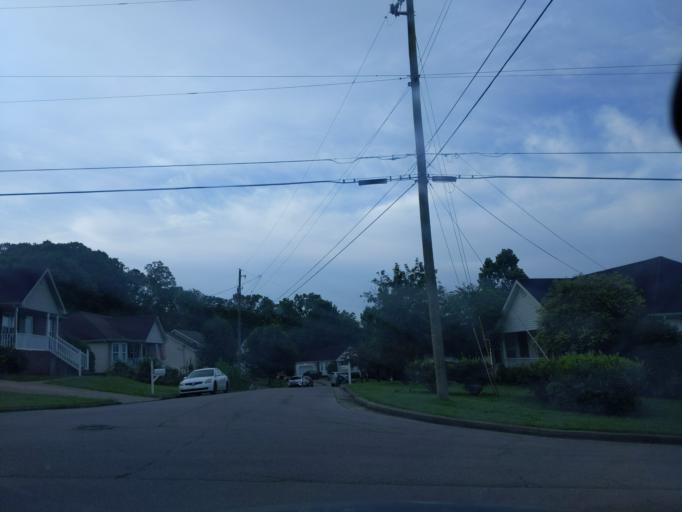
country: US
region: Tennessee
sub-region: Wilson County
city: Green Hill
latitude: 36.1778
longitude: -86.5967
